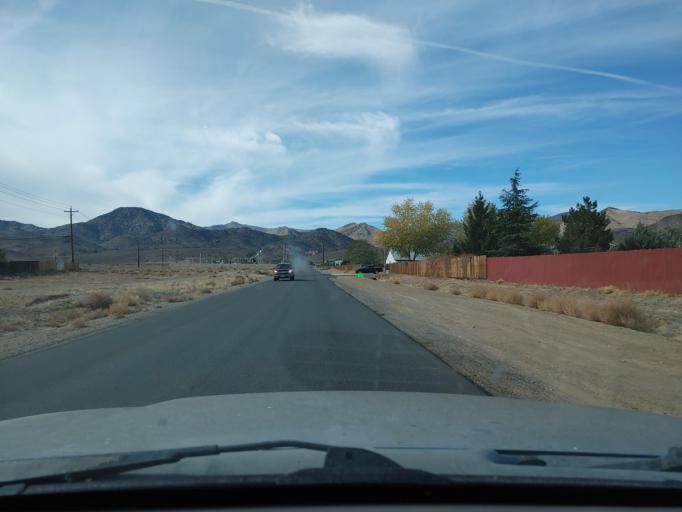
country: US
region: Nevada
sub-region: Lyon County
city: Dayton
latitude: 39.3028
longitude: -119.5419
